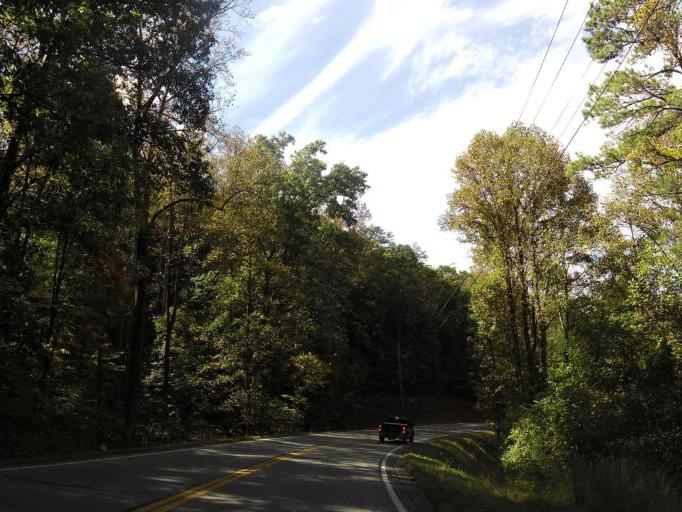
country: US
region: Georgia
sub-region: Pickens County
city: Nelson
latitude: 34.4180
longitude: -84.3204
